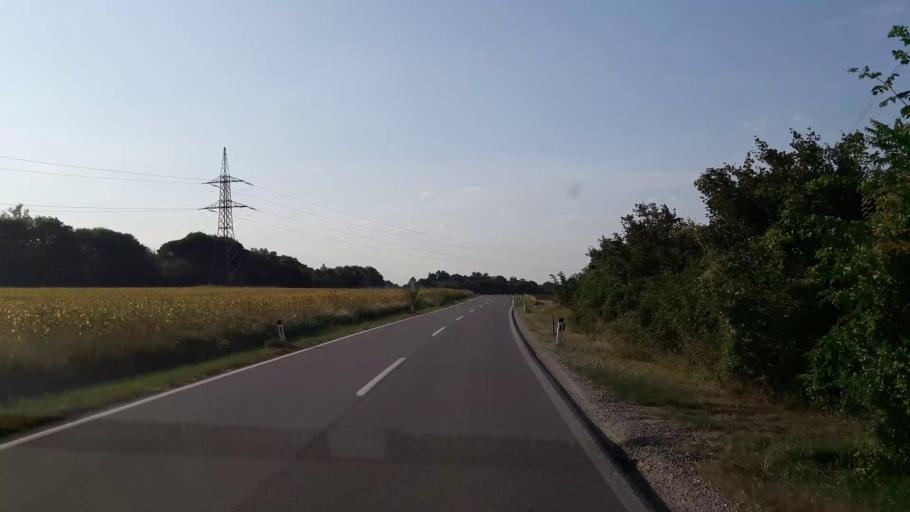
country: AT
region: Lower Austria
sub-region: Politischer Bezirk Ganserndorf
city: Orth an der Donau
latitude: 48.0825
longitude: 16.6767
